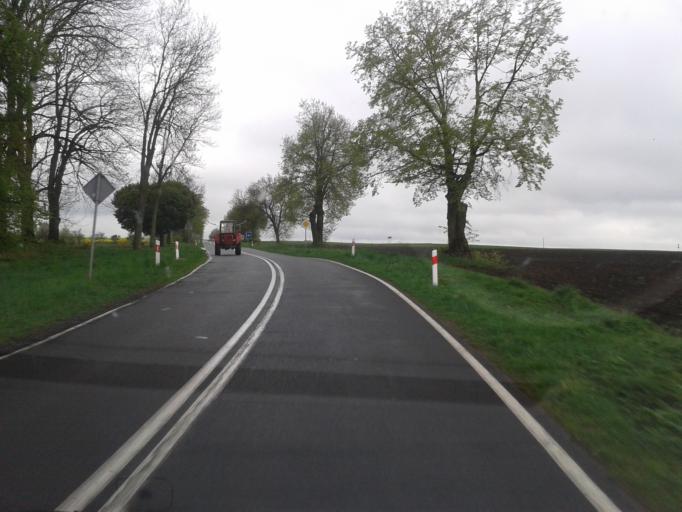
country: PL
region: Lublin Voivodeship
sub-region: Powiat tomaszowski
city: Telatyn
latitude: 50.5539
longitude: 23.9349
